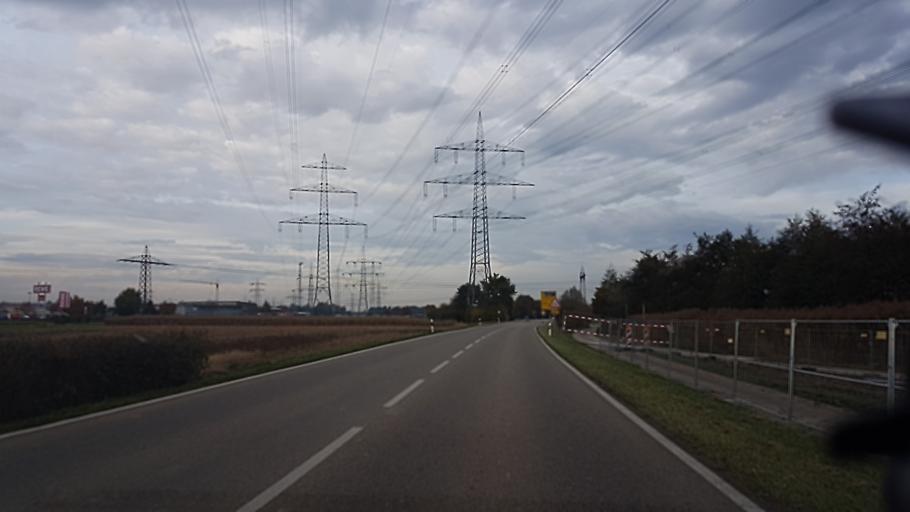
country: DE
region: Baden-Wuerttemberg
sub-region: Freiburg Region
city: Eichstetten
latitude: 48.0876
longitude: 7.7538
